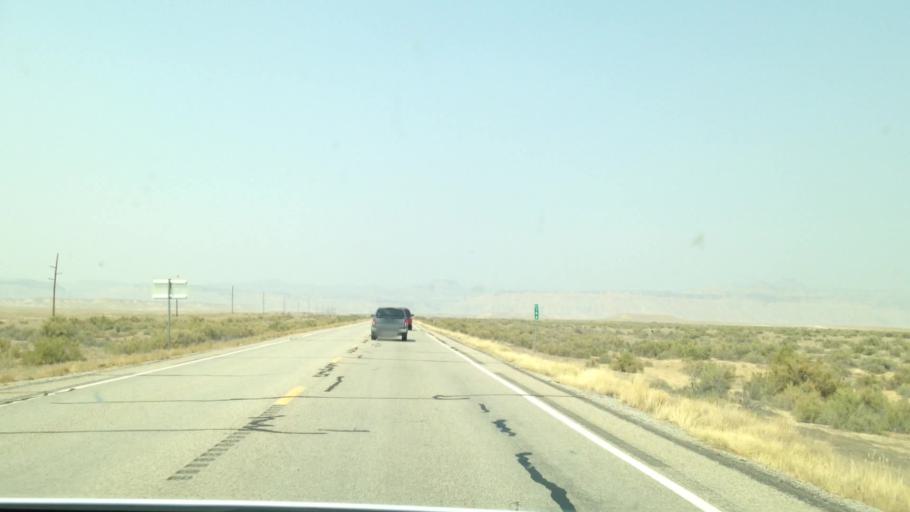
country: US
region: Utah
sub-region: Grand County
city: Moab
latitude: 38.8963
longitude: -109.8139
